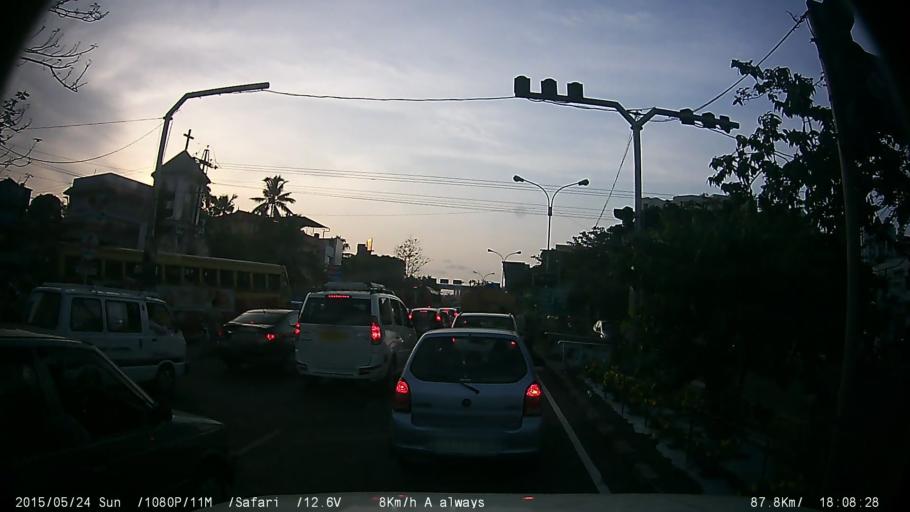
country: IN
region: Kerala
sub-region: Ernakulam
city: Elur
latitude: 10.0224
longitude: 76.3097
